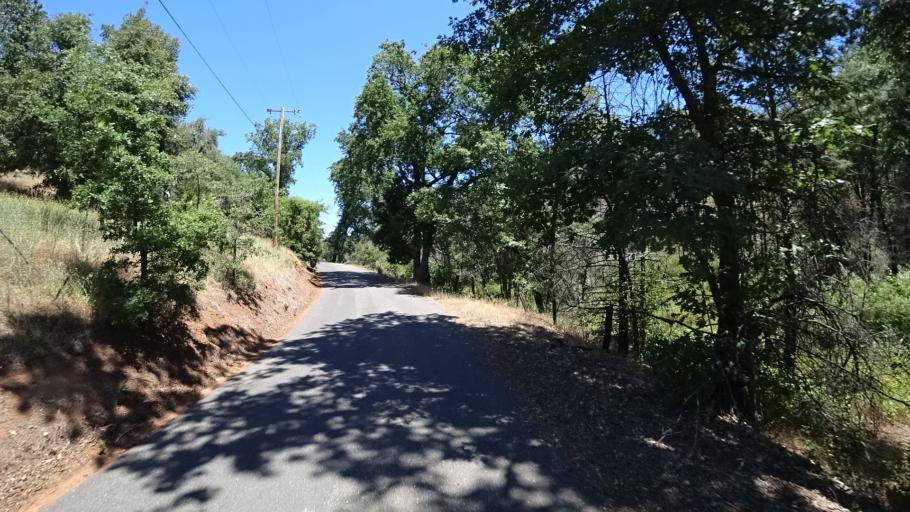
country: US
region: California
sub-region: Calaveras County
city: Mountain Ranch
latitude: 38.2446
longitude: -120.5388
